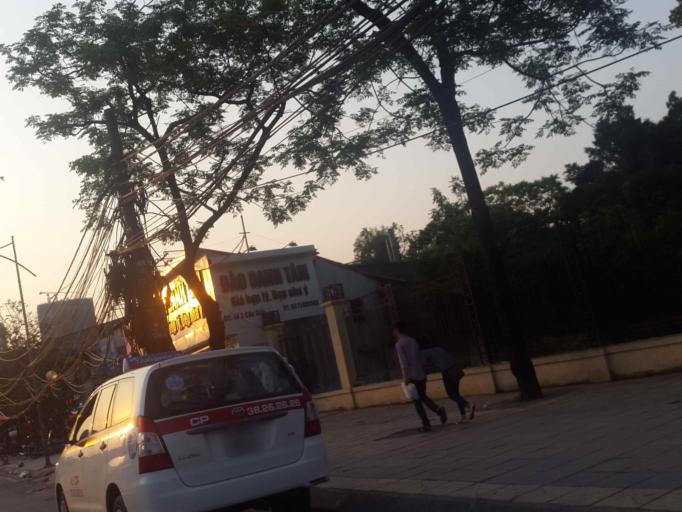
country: VN
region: Ha Noi
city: Cau Giay
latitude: 21.0293
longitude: 105.8036
